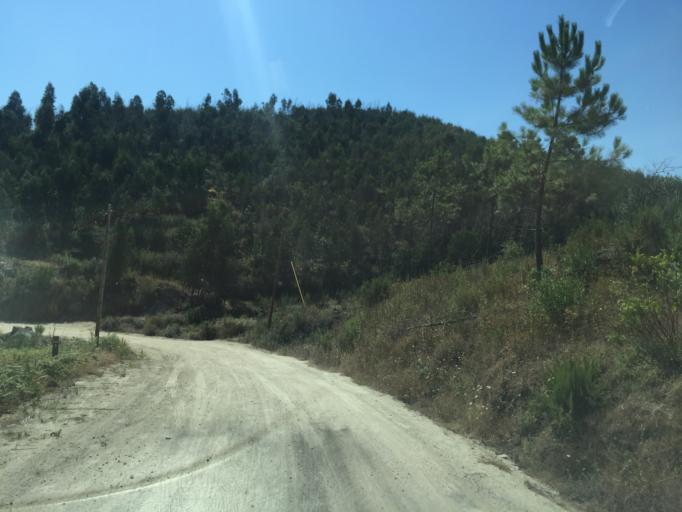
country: PT
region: Santarem
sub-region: Constancia
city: Constancia
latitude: 39.5416
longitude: -8.2804
